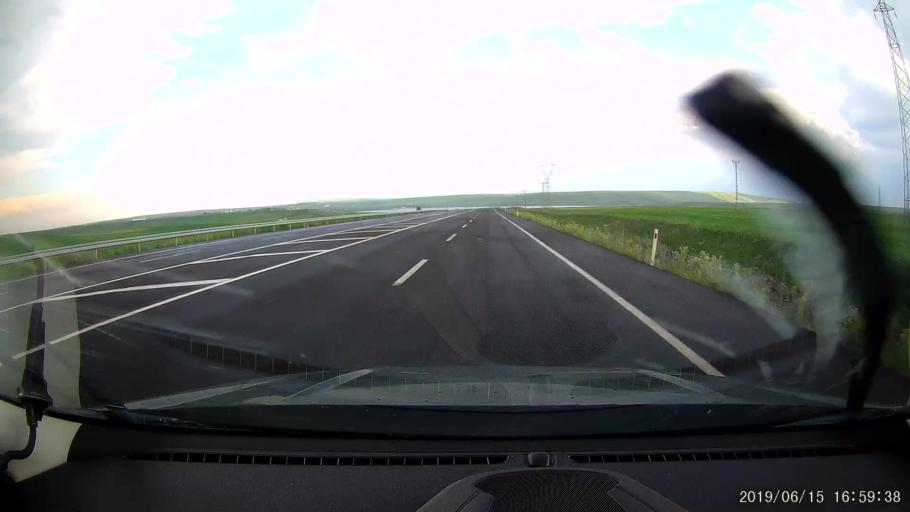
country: TR
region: Kars
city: Susuz
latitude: 40.7494
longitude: 43.1522
